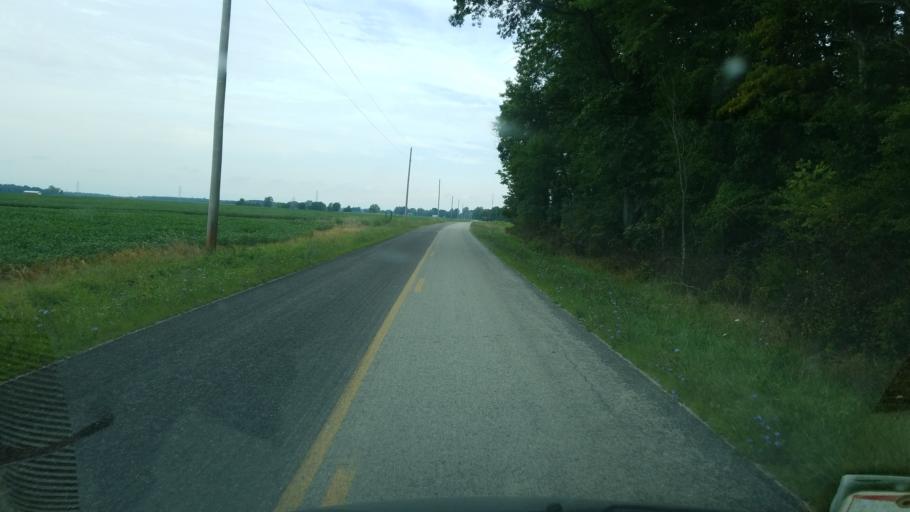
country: US
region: Ohio
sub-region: Seneca County
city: Tiffin
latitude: 41.0001
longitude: -83.0550
